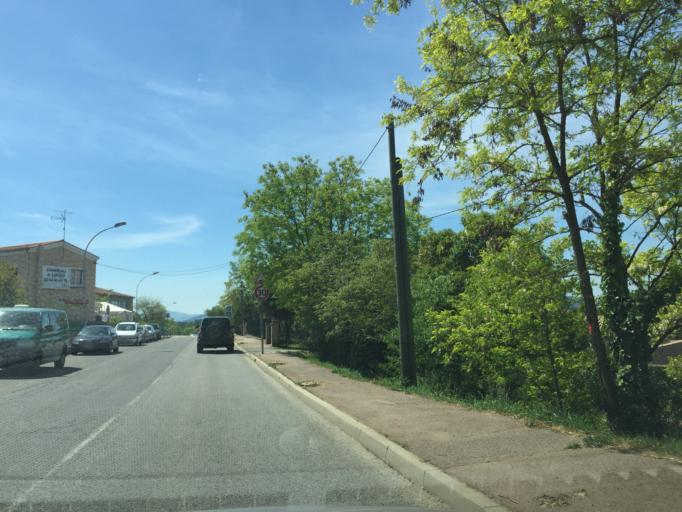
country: FR
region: Provence-Alpes-Cote d'Azur
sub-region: Departement du Var
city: Lorgues
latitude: 43.4925
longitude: 6.3541
